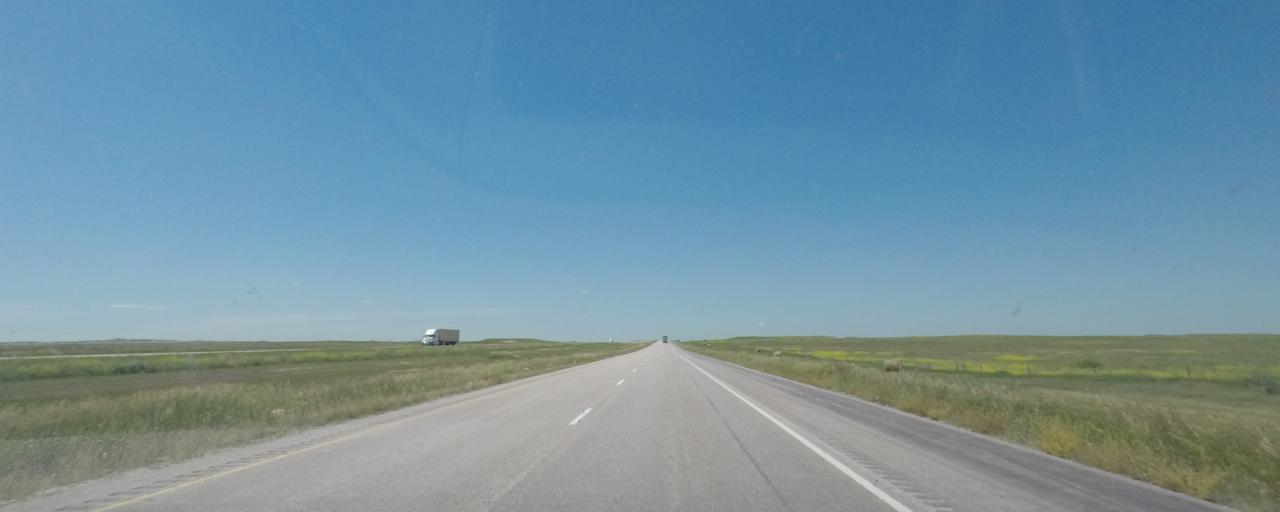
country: US
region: South Dakota
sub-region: Haakon County
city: Philip
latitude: 43.9449
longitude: -102.1598
